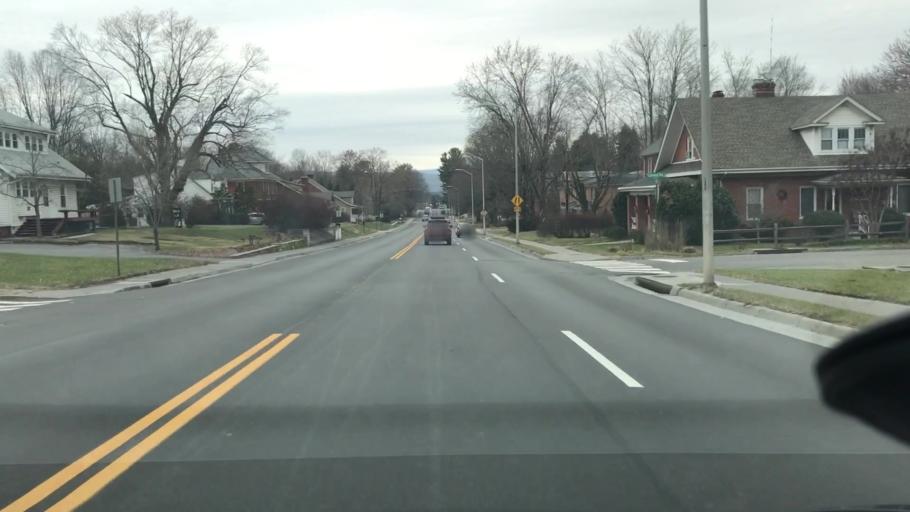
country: US
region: Virginia
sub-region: Montgomery County
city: Blacksburg
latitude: 37.2230
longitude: -80.4070
